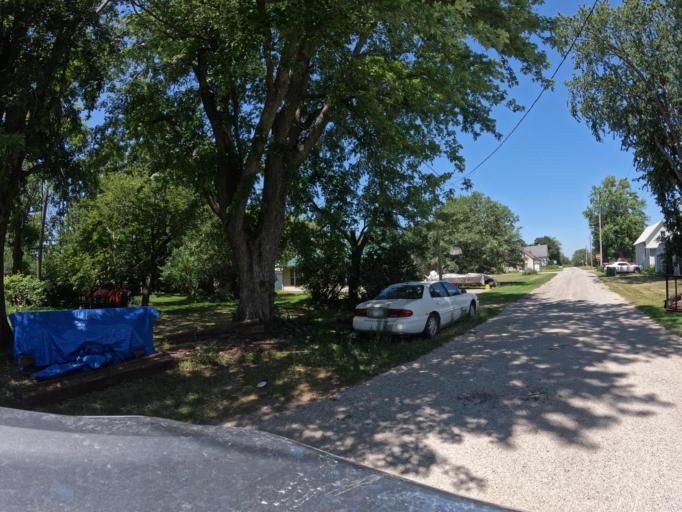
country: US
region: Iowa
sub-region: Keokuk County
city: Sigourney
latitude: 41.4538
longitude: -92.3343
